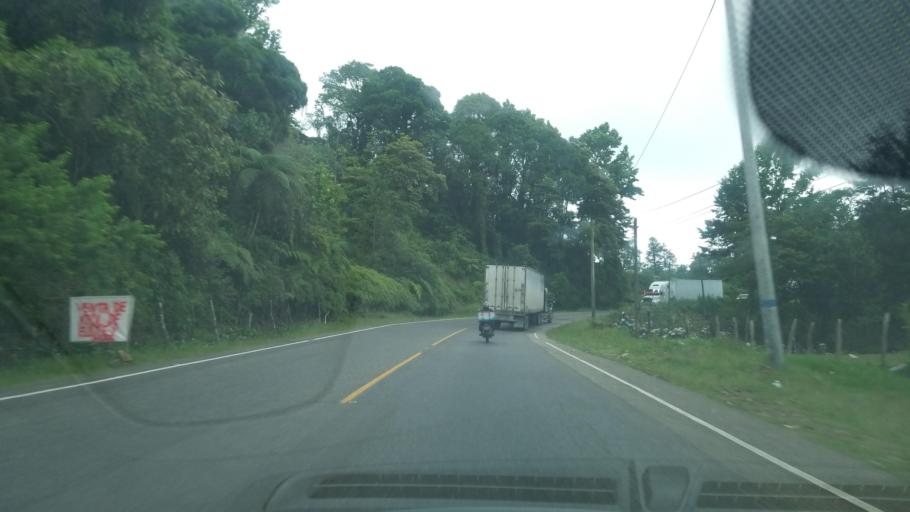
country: HN
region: Ocotepeque
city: La Labor
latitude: 14.4720
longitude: -89.0616
